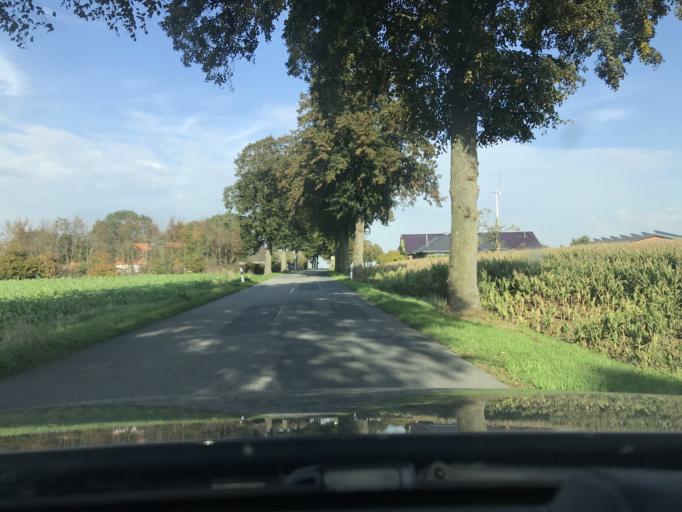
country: DE
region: North Rhine-Westphalia
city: Kalkar
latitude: 51.7126
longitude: 6.2687
